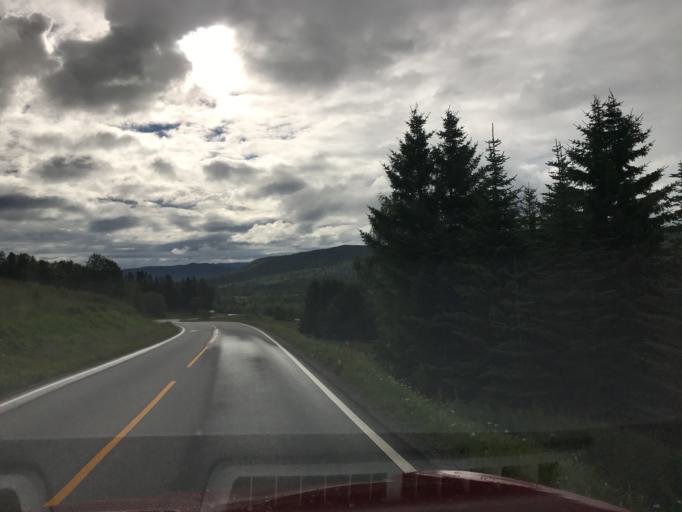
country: NO
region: Buskerud
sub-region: Hol
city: Hol
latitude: 60.4125
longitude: 8.4270
